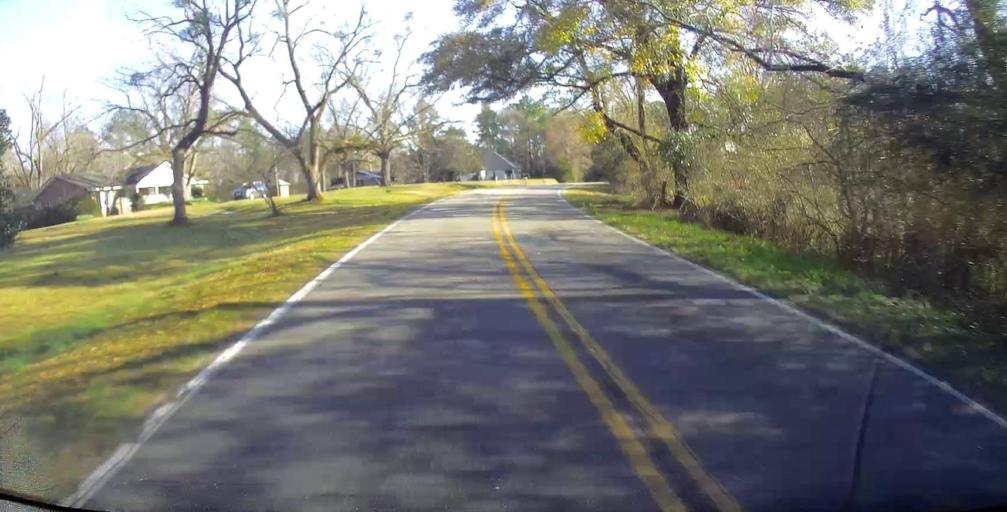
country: US
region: Georgia
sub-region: Harris County
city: Hamilton
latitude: 32.5569
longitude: -84.7801
